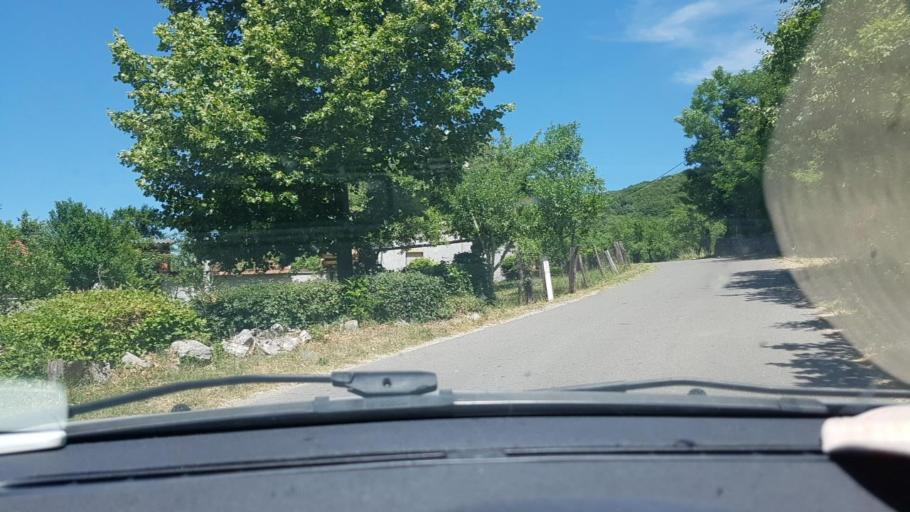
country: HR
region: Licko-Senjska
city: Otocac
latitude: 44.7905
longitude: 15.3678
